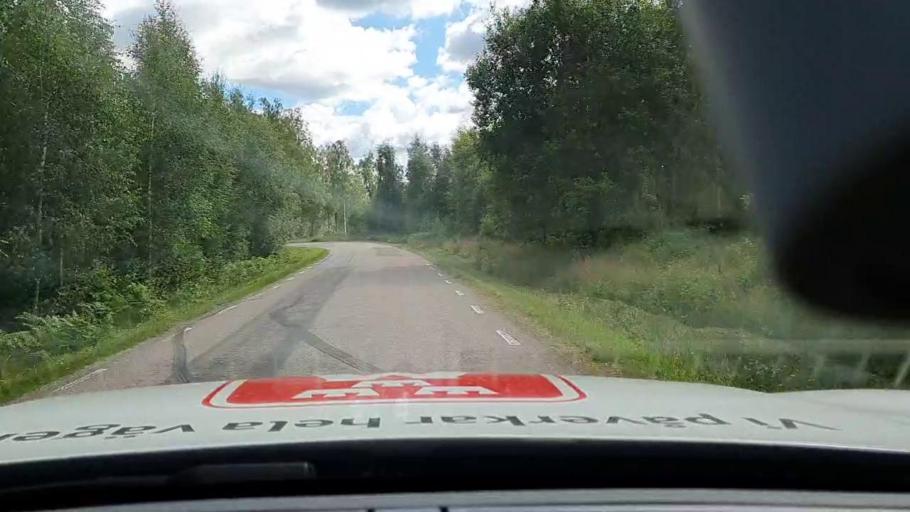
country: SE
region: Vaestra Goetaland
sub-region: Karlsborgs Kommun
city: Molltorp
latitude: 58.6052
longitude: 14.3024
